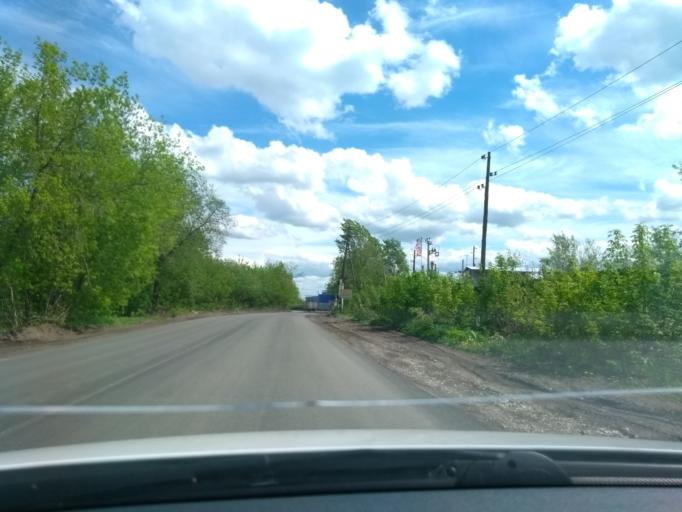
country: RU
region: Perm
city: Kondratovo
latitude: 58.0087
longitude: 56.0838
